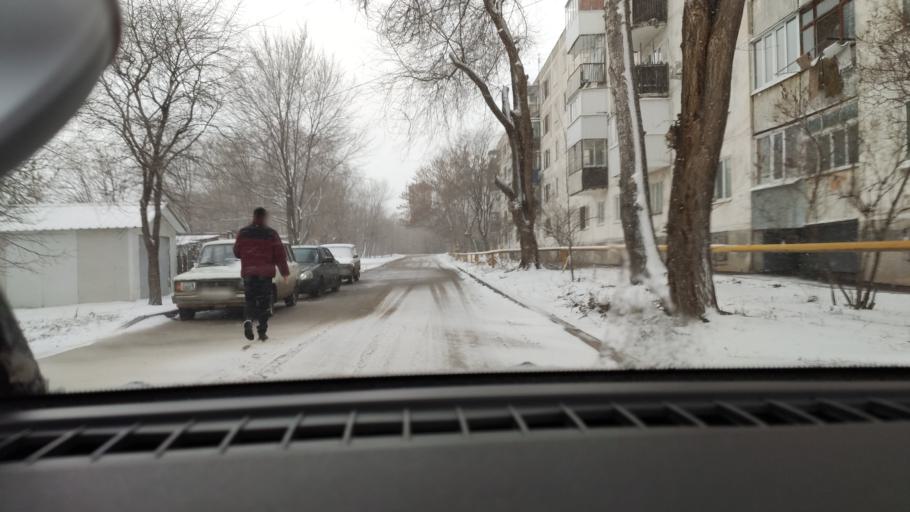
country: RU
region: Samara
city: Samara
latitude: 53.1372
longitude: 50.1580
